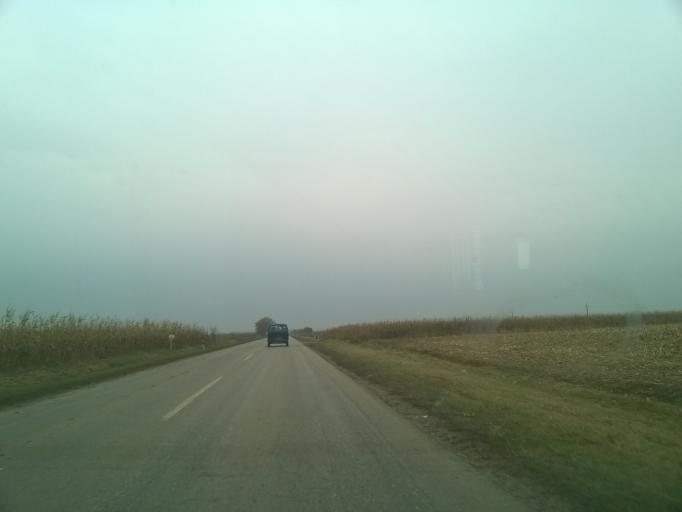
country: RS
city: Crepaja
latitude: 45.0321
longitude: 20.6384
